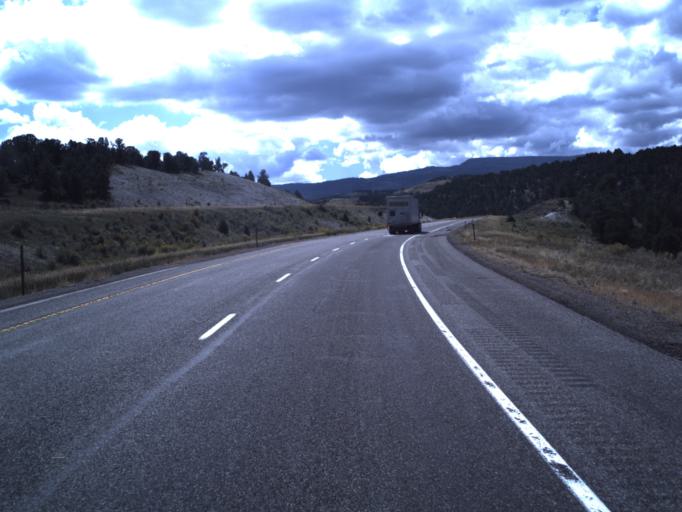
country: US
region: Utah
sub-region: Sevier County
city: Salina
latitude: 38.8658
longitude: -111.5521
